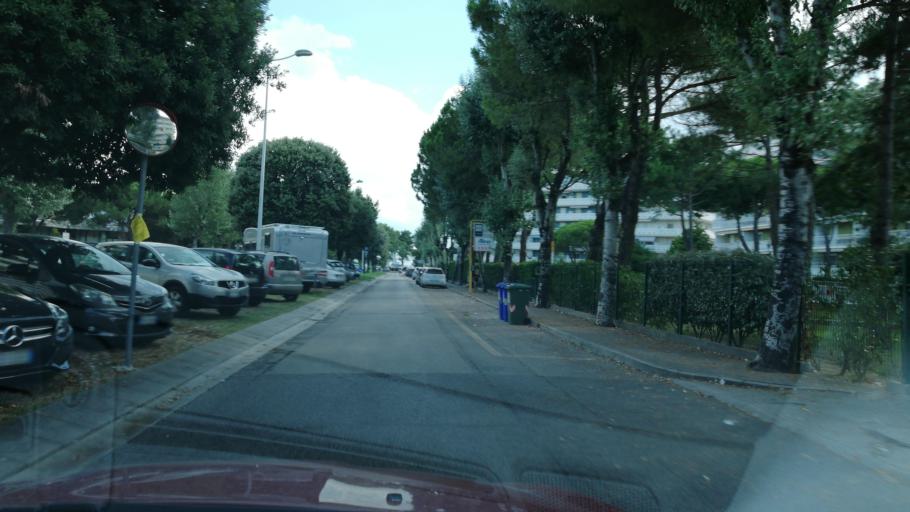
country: IT
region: Veneto
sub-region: Provincia di Venezia
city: Caorle
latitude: 45.5865
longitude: 12.8516
